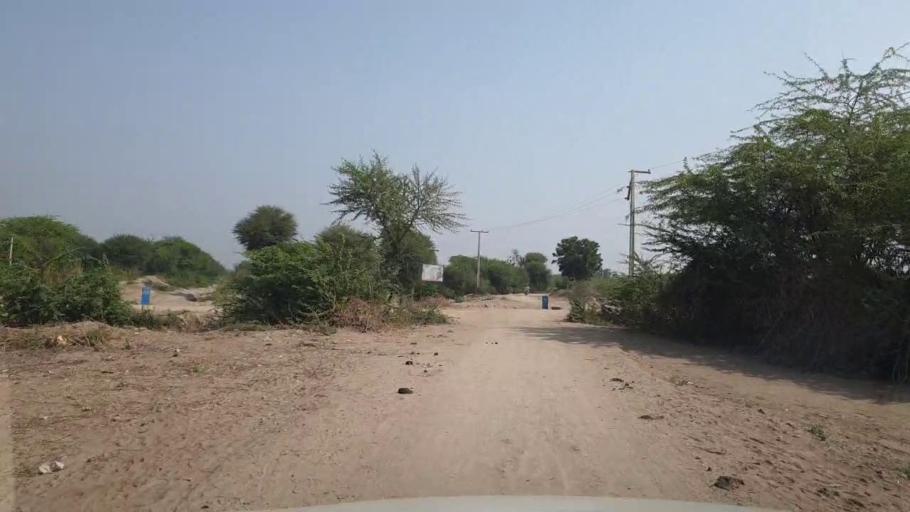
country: PK
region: Sindh
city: Chor
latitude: 25.4618
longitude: 69.7077
